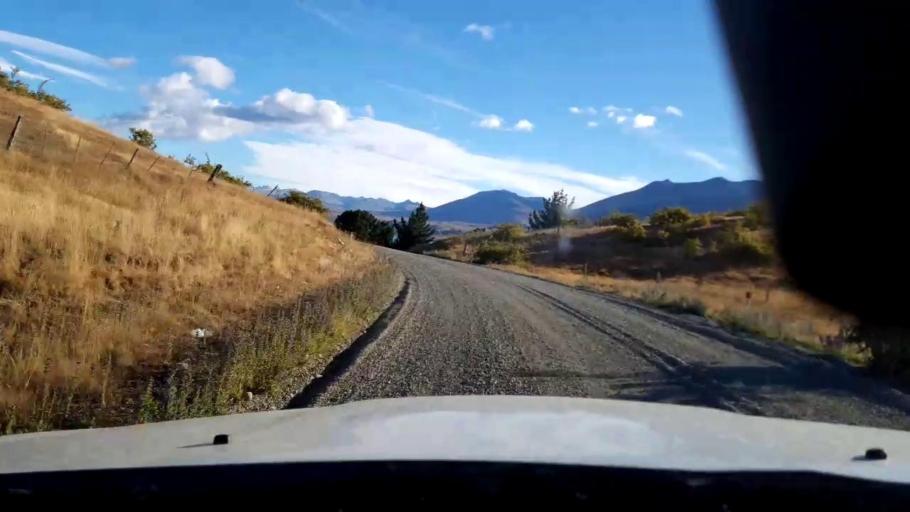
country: NZ
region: Canterbury
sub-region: Timaru District
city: Pleasant Point
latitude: -43.9652
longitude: 170.5220
